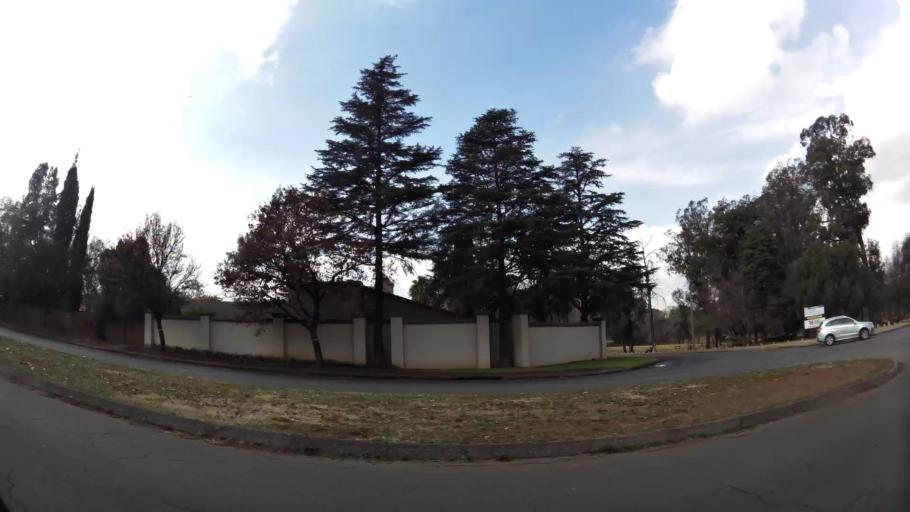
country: ZA
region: Gauteng
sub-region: Sedibeng District Municipality
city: Vanderbijlpark
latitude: -26.7300
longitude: 27.8374
